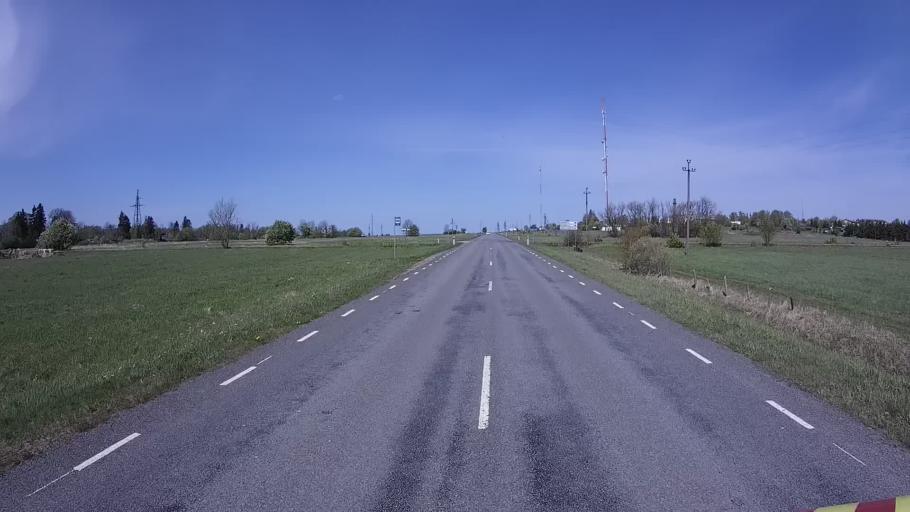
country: EE
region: Laeaene
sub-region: Lihula vald
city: Lihula
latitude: 58.6713
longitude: 23.8266
